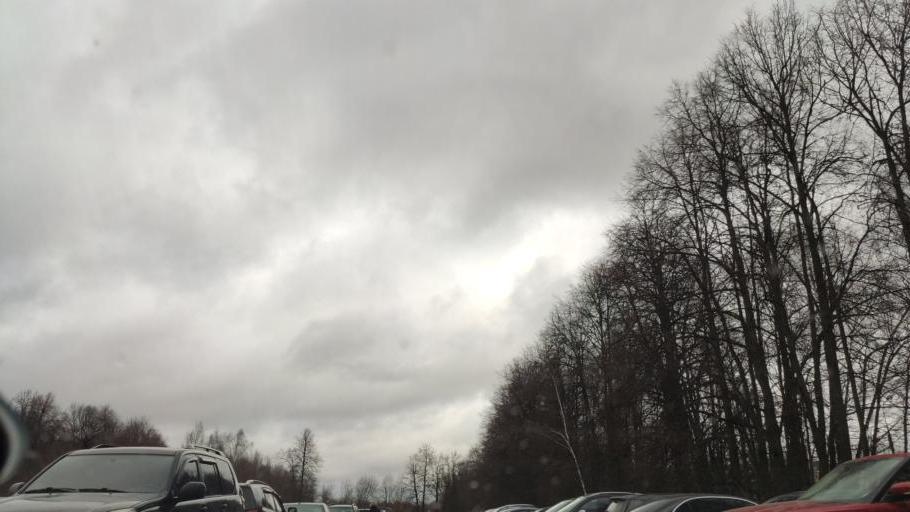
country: RU
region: Moscow
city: Yasenevo
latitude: 55.6151
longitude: 37.5300
